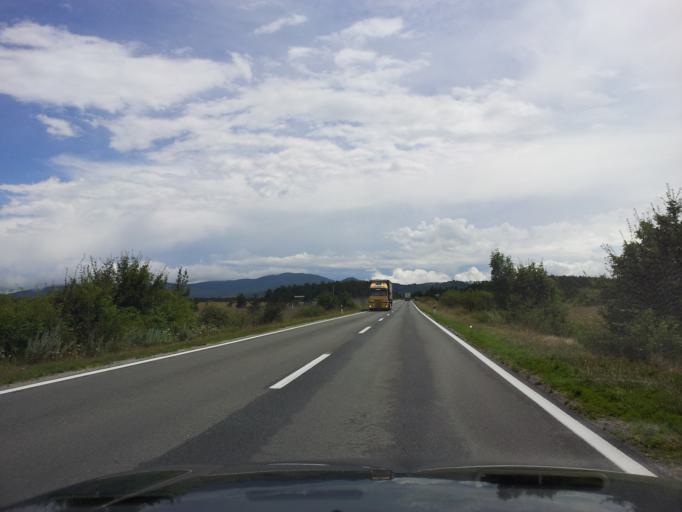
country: BA
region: Federation of Bosnia and Herzegovina
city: Bihac
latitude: 44.5648
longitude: 15.7559
